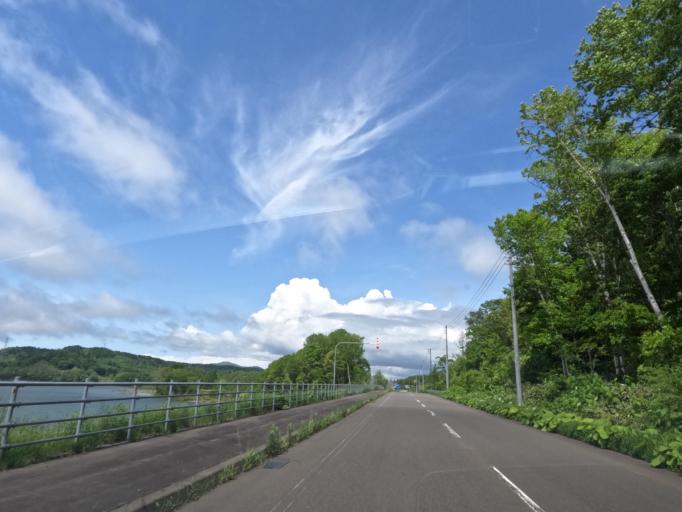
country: JP
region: Hokkaido
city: Tobetsu
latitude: 43.3655
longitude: 141.5723
